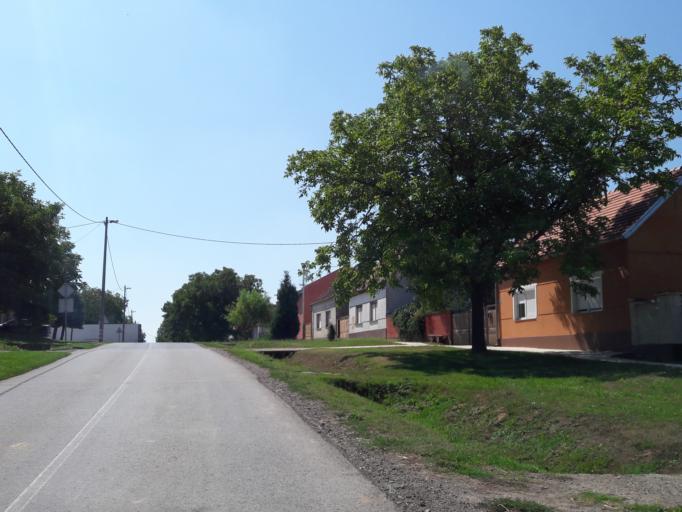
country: HR
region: Osjecko-Baranjska
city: Gorjani
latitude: 45.3721
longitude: 18.4077
